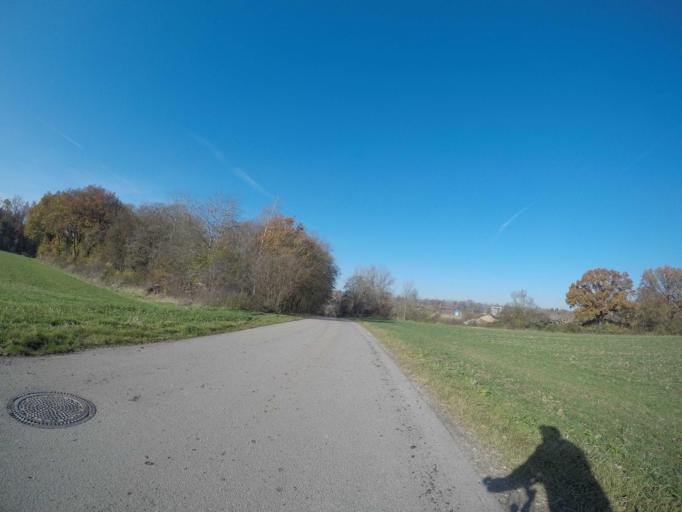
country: DE
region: Baden-Wuerttemberg
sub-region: Tuebingen Region
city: Riedlingen
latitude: 48.1634
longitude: 9.4954
